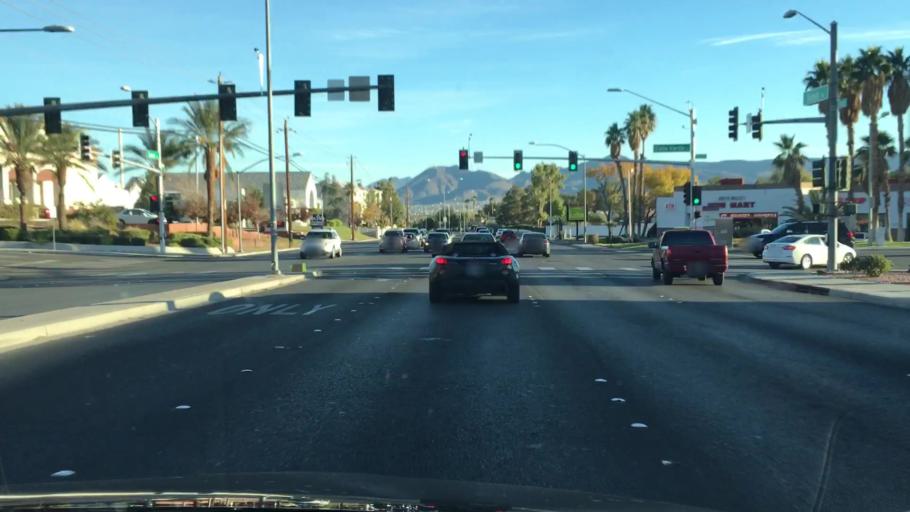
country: US
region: Nevada
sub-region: Clark County
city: Whitney
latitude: 36.0683
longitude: -115.0685
